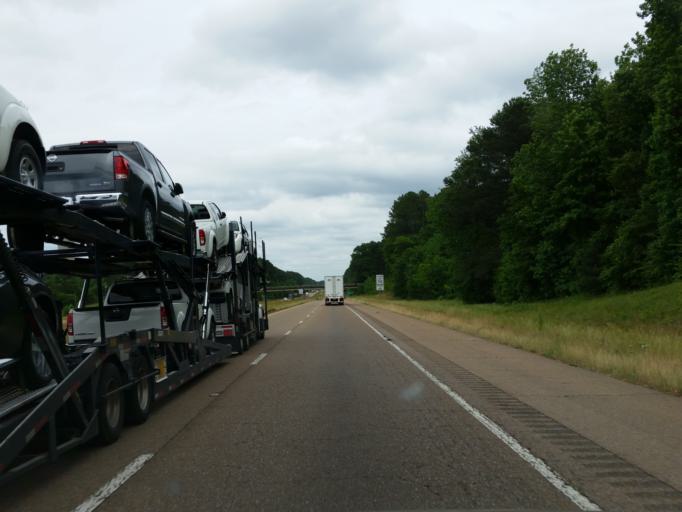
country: US
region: Mississippi
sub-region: Lauderdale County
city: Marion
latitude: 32.3852
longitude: -88.6256
